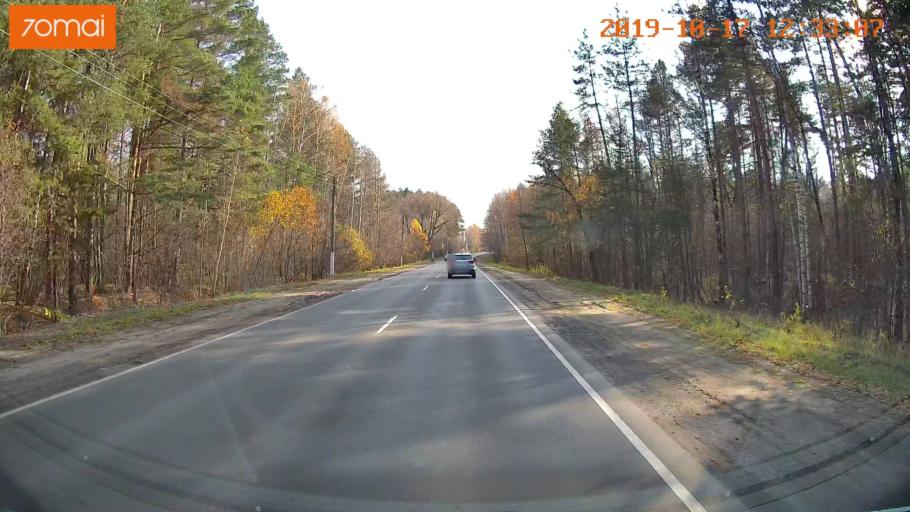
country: RU
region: Rjazan
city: Kasimov
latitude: 54.9573
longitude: 41.3504
